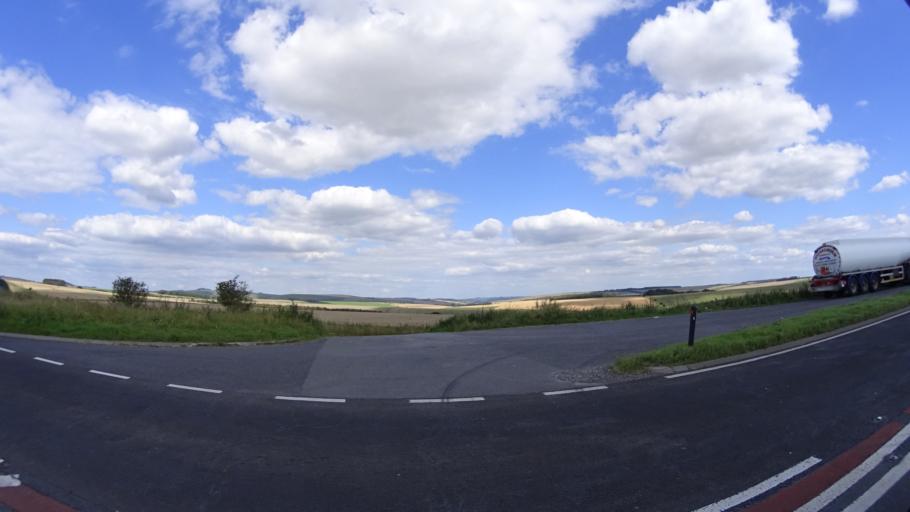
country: GB
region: England
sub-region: Wiltshire
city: Mere
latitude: 51.1038
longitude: -2.2104
